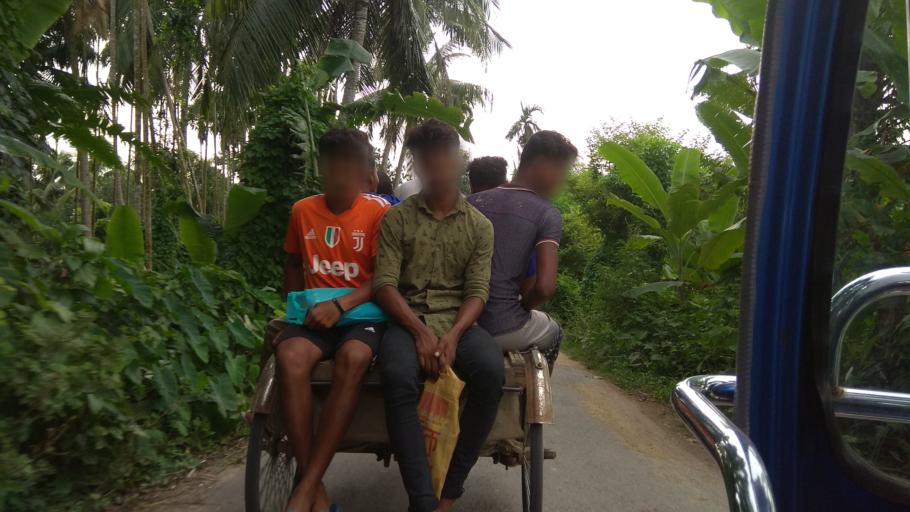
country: BD
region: Khulna
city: Kalia
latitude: 23.0314
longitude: 89.6481
